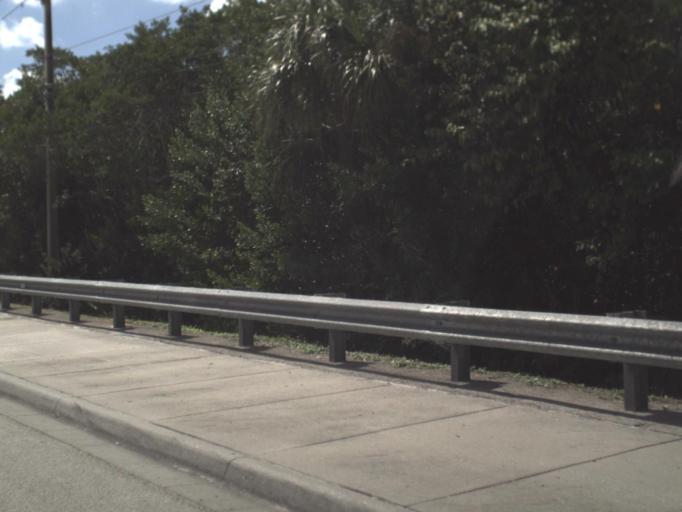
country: US
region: Florida
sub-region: Collier County
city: Naples Park
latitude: 26.2866
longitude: -81.8020
